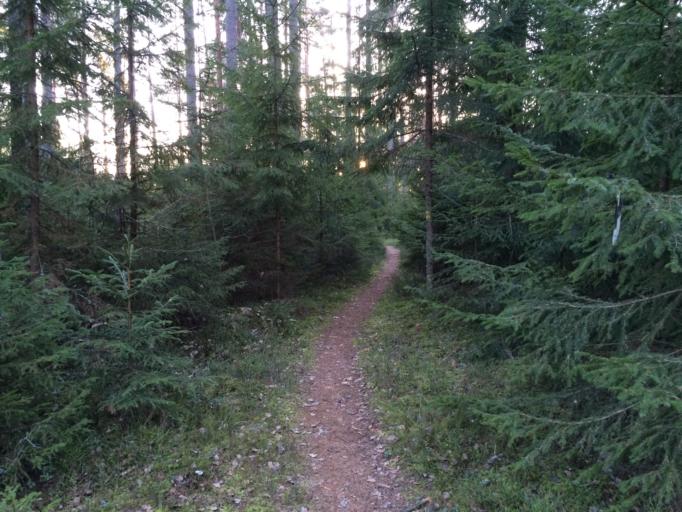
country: SE
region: Vaestmanland
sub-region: Hallstahammars Kommun
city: Hallstahammar
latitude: 59.6226
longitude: 16.1970
